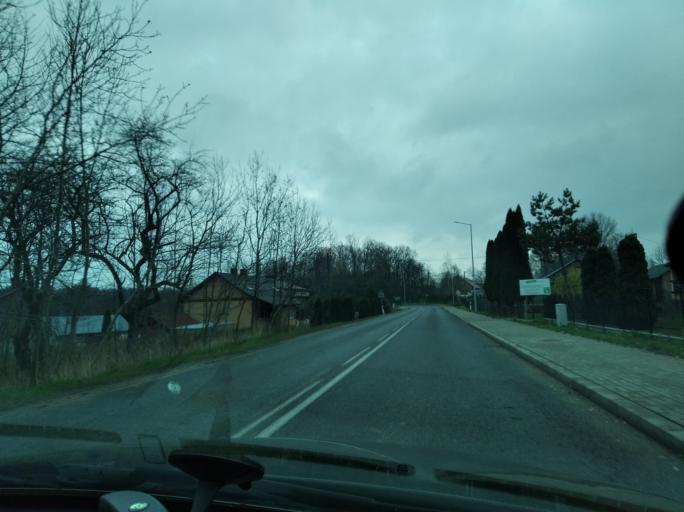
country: PL
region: Subcarpathian Voivodeship
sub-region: Powiat przeworski
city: Sietesz
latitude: 50.0008
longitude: 22.3509
